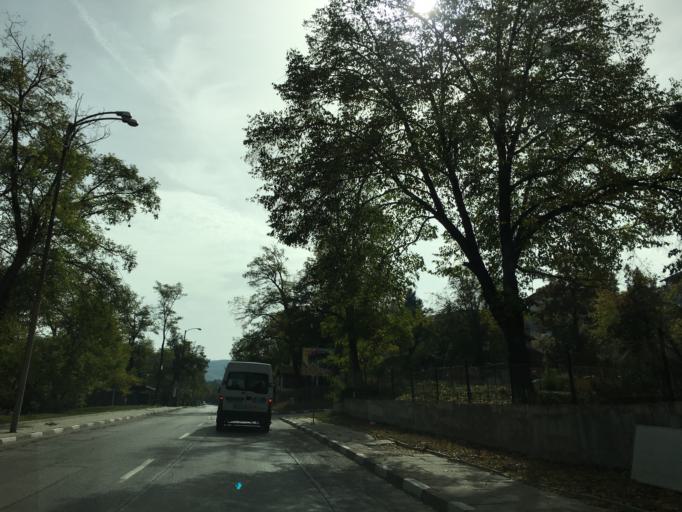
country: BG
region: Sofia-Capital
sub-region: Stolichna Obshtina
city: Sofia
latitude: 42.5886
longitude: 23.4195
